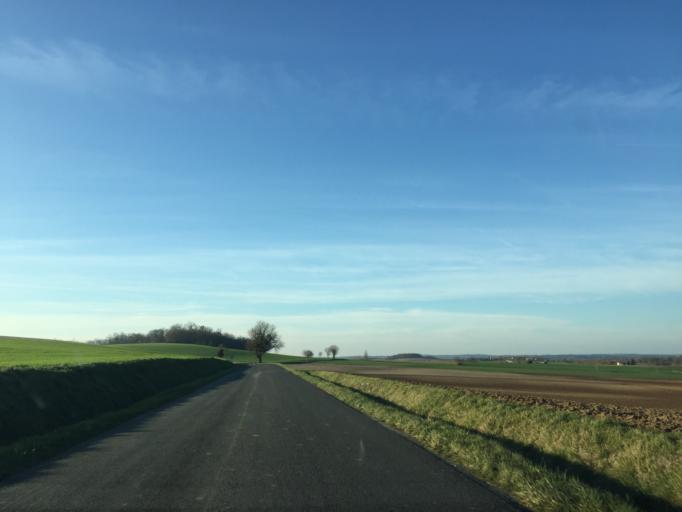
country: FR
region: Aquitaine
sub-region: Departement de la Dordogne
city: Riberac
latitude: 45.2356
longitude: 0.2565
